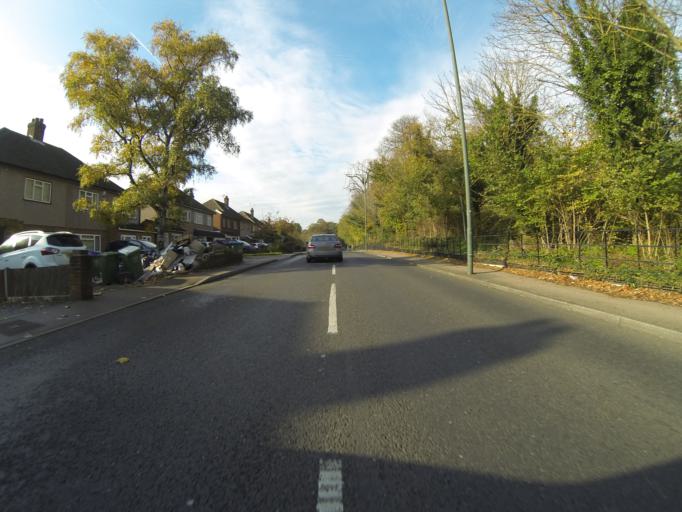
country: GB
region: England
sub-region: Greater London
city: Bexley
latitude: 51.4523
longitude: 0.1708
